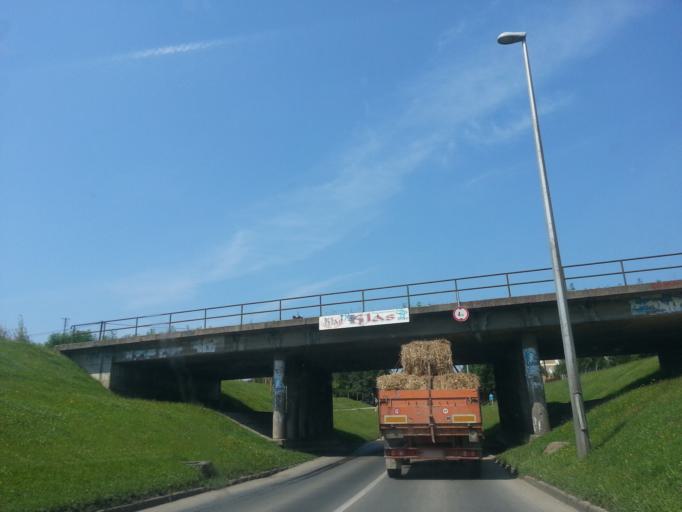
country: BA
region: Brcko
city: Brcko
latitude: 44.8653
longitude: 18.8112
